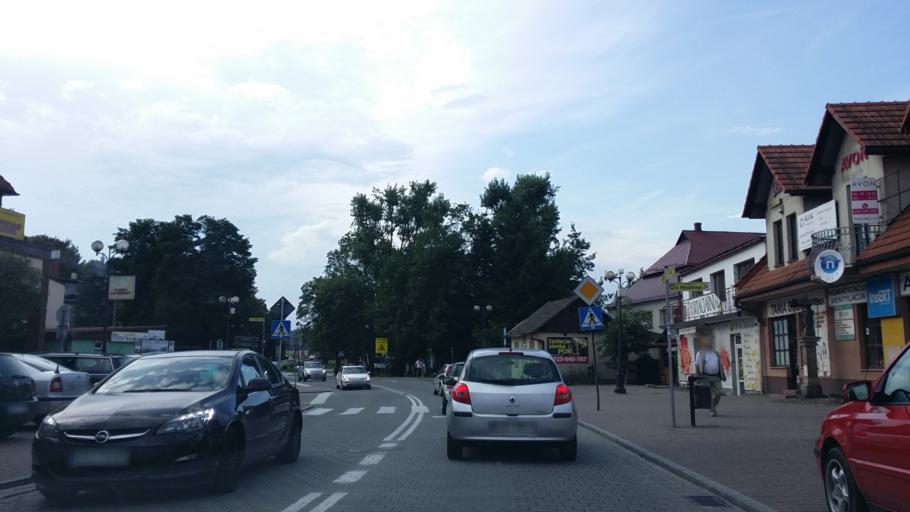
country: PL
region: Lesser Poland Voivodeship
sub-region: Powiat myslenicki
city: Dobczyce
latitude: 49.8810
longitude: 20.0896
